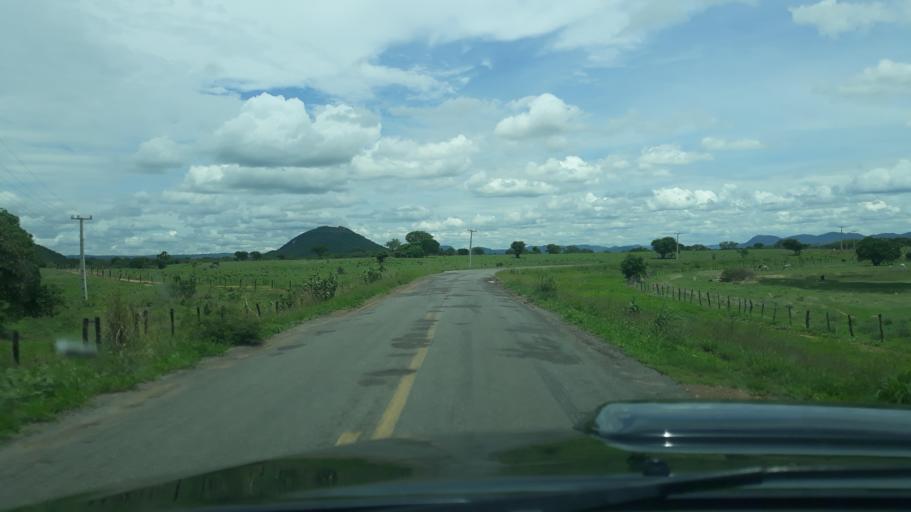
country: BR
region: Bahia
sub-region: Guanambi
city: Guanambi
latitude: -14.1563
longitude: -42.8197
